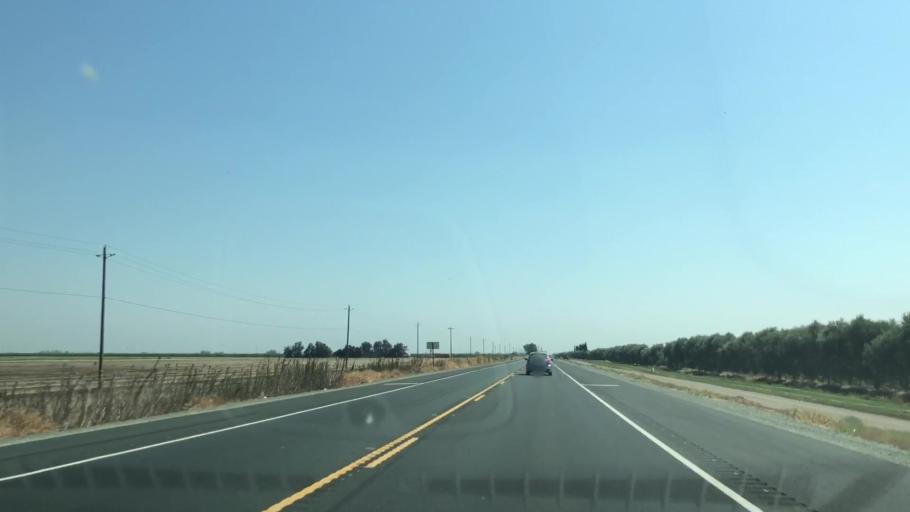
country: US
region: California
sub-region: San Joaquin County
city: Thornton
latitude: 38.1154
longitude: -121.4558
